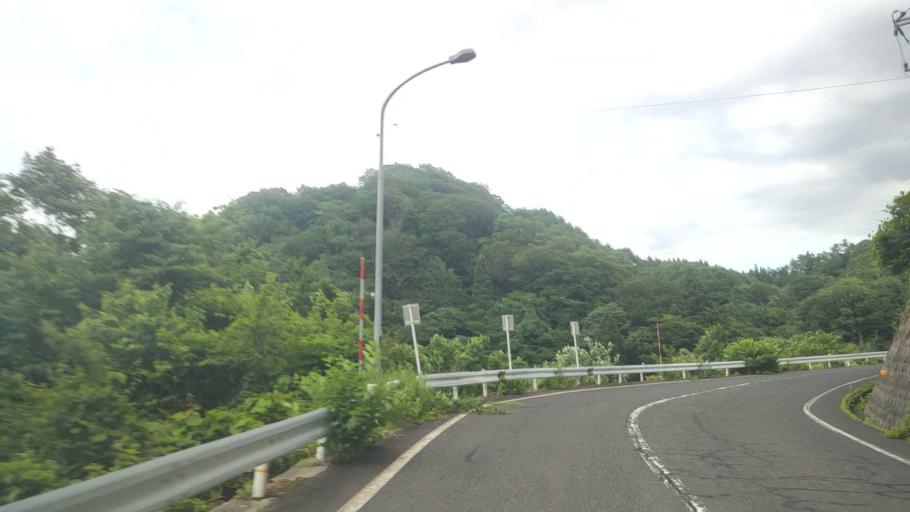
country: JP
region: Tottori
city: Kurayoshi
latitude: 35.3194
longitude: 134.0094
